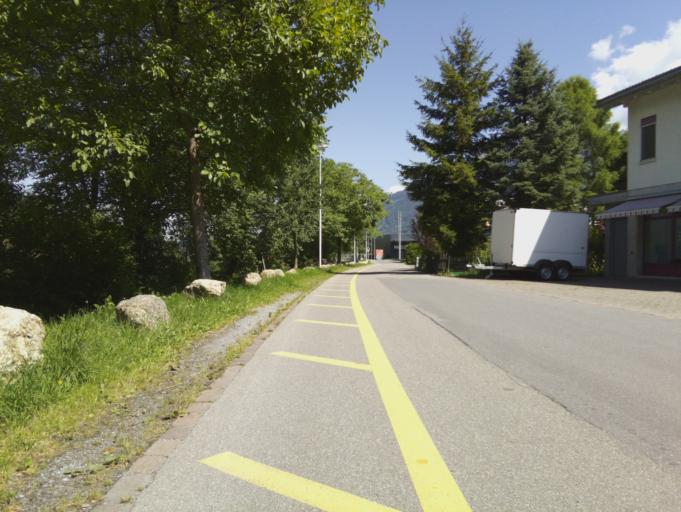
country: CH
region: Glarus
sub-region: Glarus
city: Oberurnen
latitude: 47.1096
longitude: 9.0665
